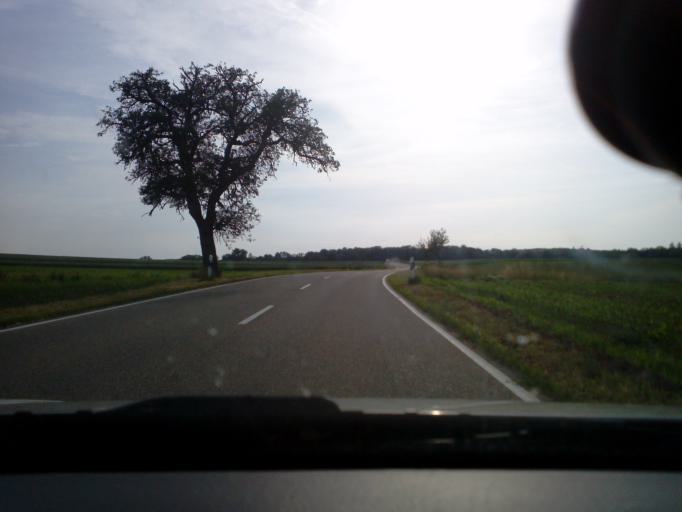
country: DE
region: Baden-Wuerttemberg
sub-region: Karlsruhe Region
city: Maulbronn
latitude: 49.0082
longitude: 8.8393
